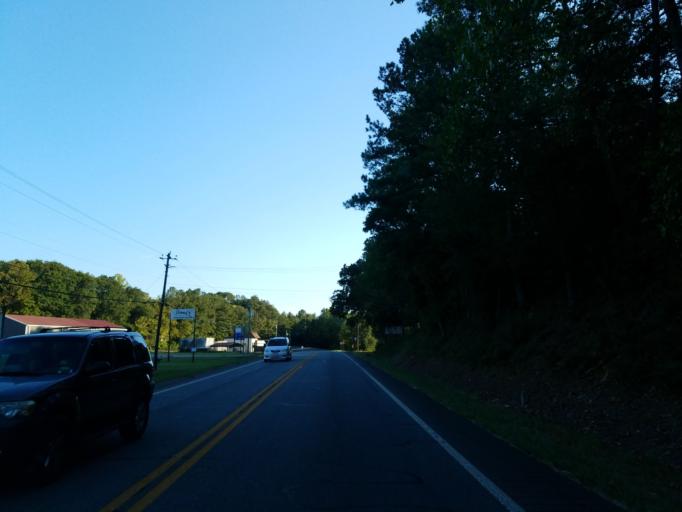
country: US
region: Georgia
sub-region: Bartow County
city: Rydal
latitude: 34.4302
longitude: -84.7004
